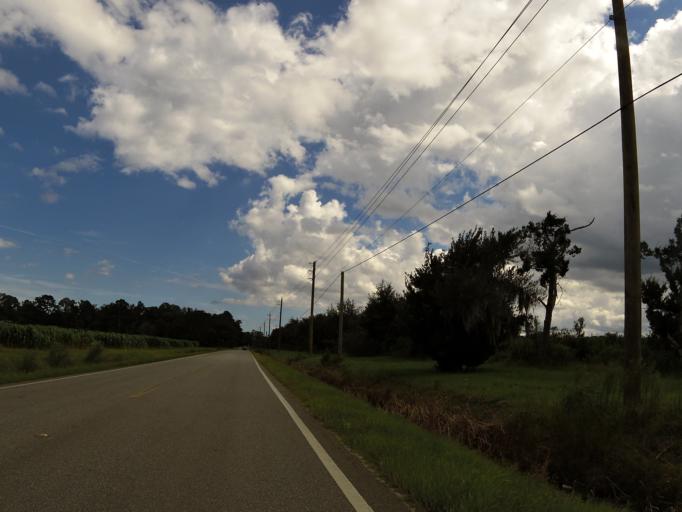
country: US
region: Florida
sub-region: Saint Johns County
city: Saint Augustine South
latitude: 29.8235
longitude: -81.4900
